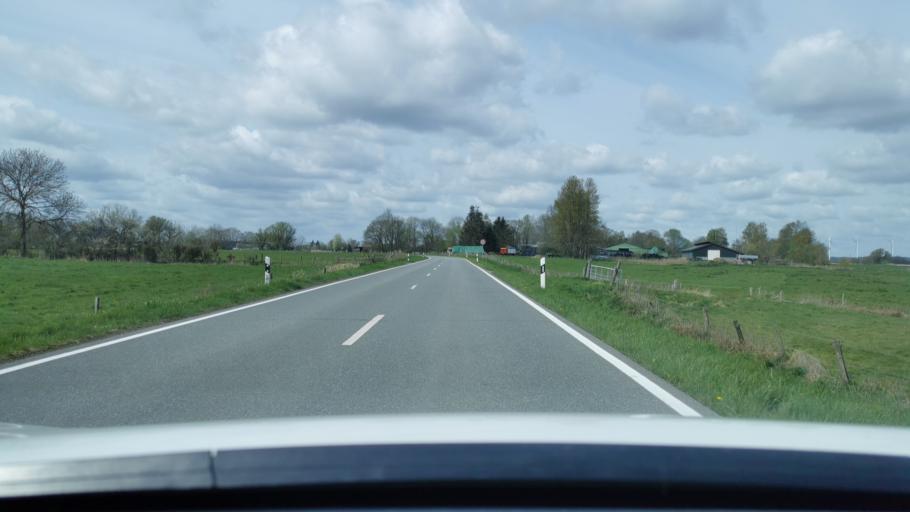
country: DE
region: Schleswig-Holstein
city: Prinzenmoor
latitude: 54.1929
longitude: 9.4591
